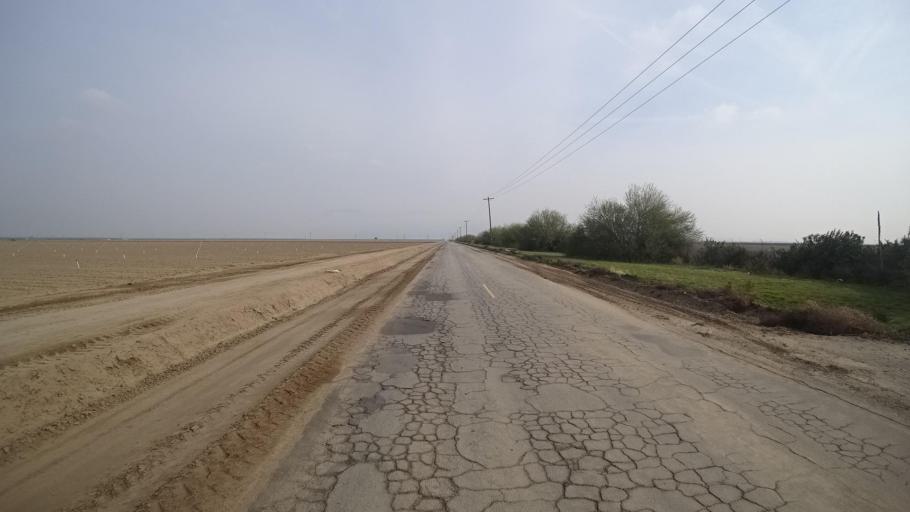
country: US
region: California
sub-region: Kern County
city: Arvin
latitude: 35.1507
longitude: -118.8862
